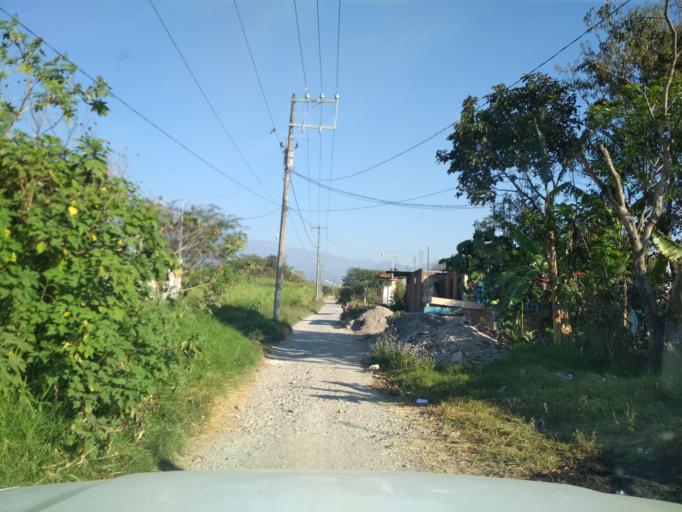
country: MX
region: Veracruz
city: Jalapilla
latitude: 18.8263
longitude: -97.0790
